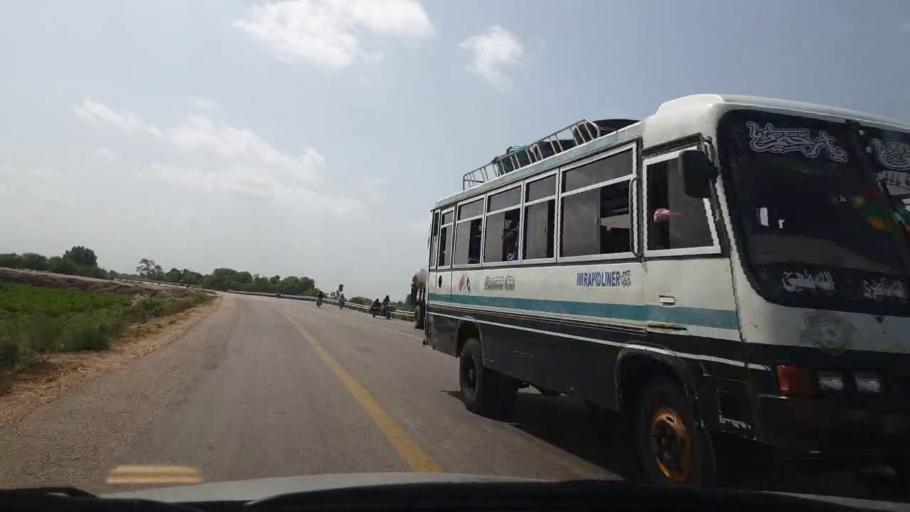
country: PK
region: Sindh
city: Matli
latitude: 24.9663
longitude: 68.6807
